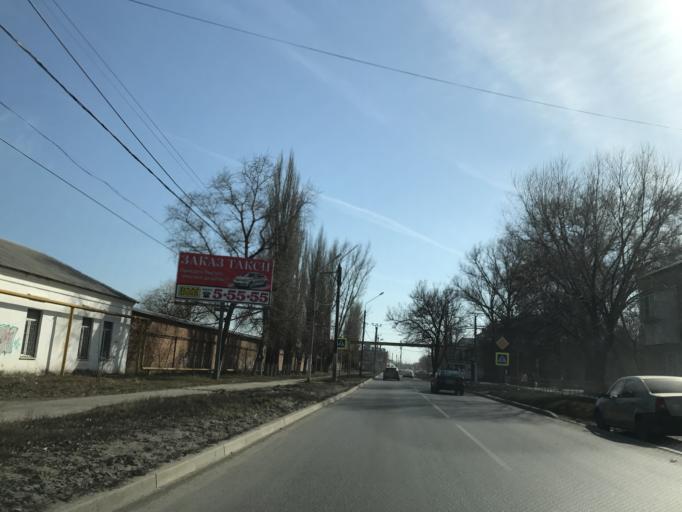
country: RU
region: Rostov
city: Bataysk
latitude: 47.1345
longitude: 39.7418
